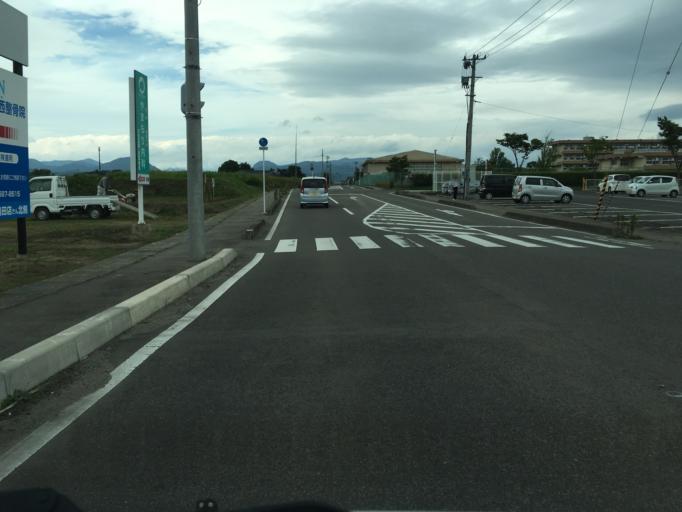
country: JP
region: Fukushima
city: Fukushima-shi
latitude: 37.7712
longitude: 140.4344
